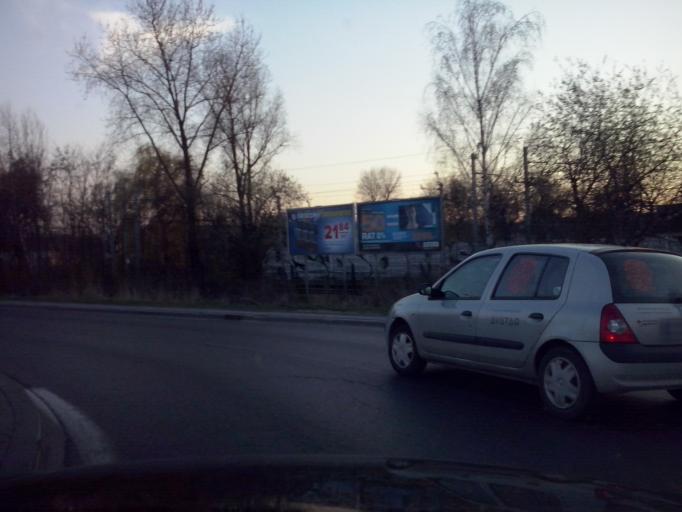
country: PL
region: Lesser Poland Voivodeship
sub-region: Krakow
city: Krakow
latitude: 50.0761
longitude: 19.9456
